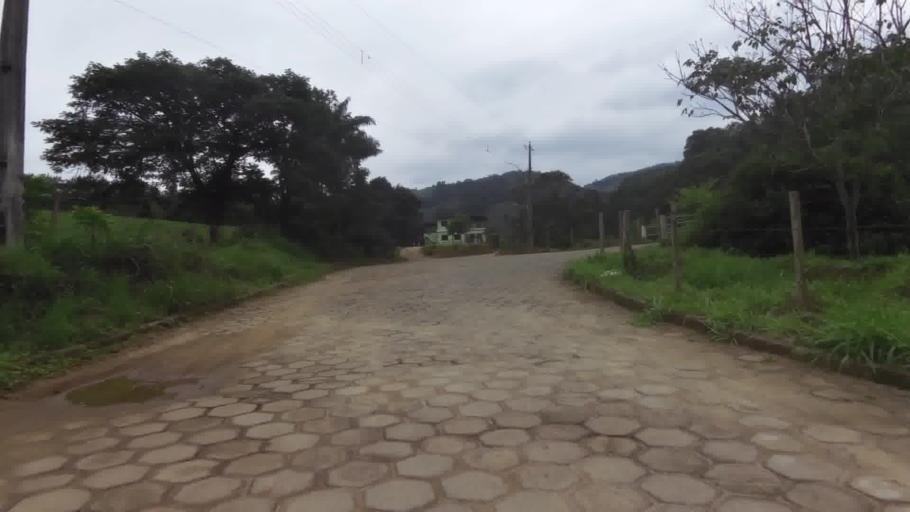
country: BR
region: Espirito Santo
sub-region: Iconha
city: Iconha
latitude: -20.7782
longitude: -40.8289
